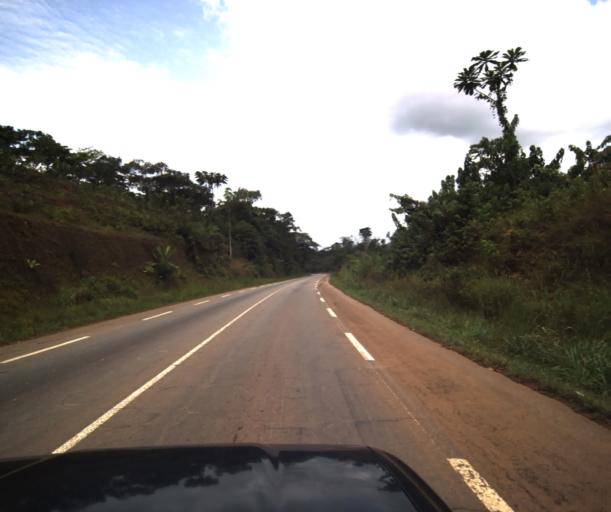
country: CM
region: Centre
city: Mbankomo
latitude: 3.7621
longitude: 11.1000
